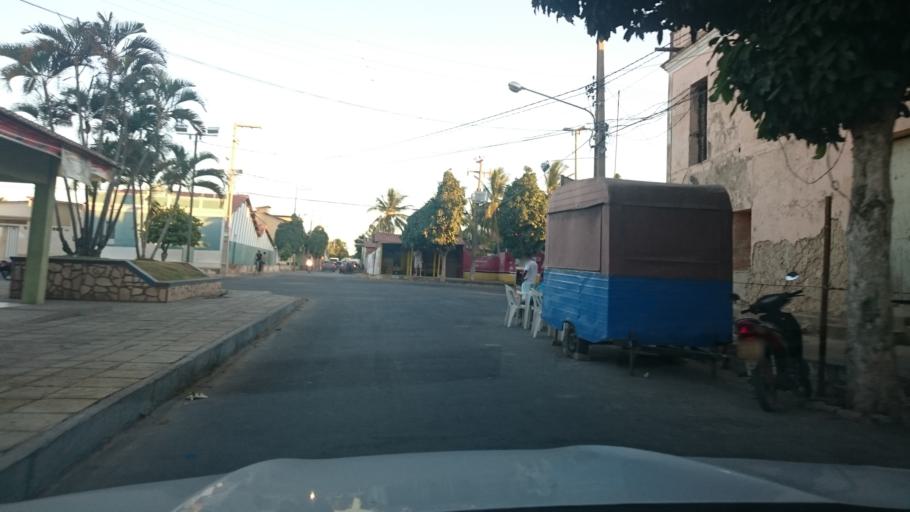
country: BR
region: Rio Grande do Norte
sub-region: Umarizal
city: Umarizal
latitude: -6.0247
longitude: -37.9874
